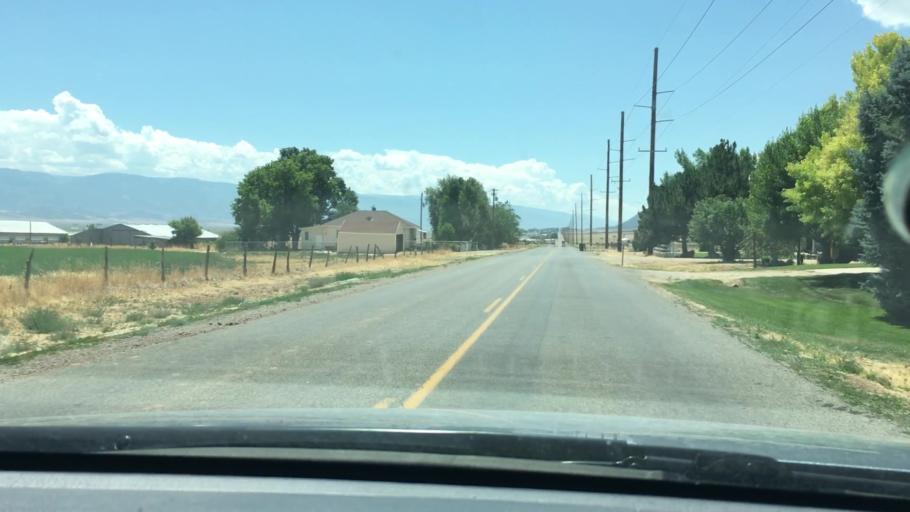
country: US
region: Utah
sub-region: Sanpete County
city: Moroni
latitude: 39.5435
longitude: -111.6400
